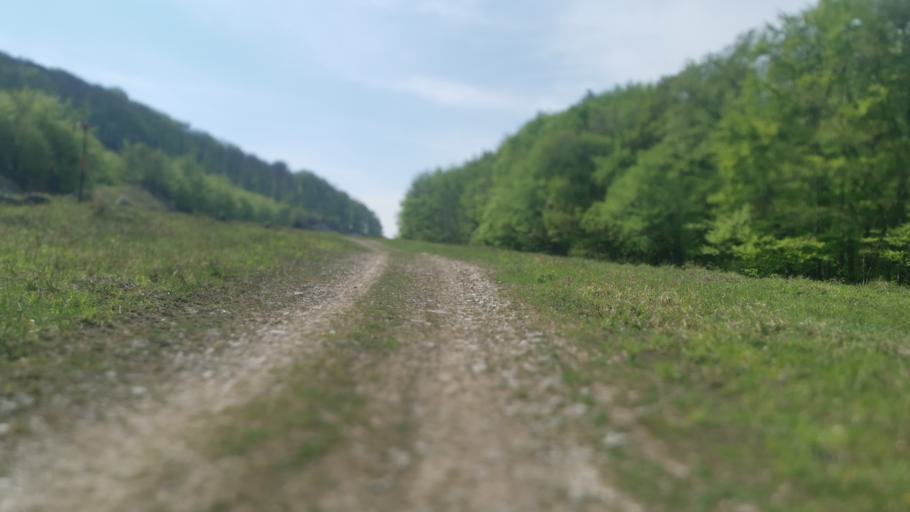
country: SK
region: Trnavsky
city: Smolenice
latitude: 48.5318
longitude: 17.4173
